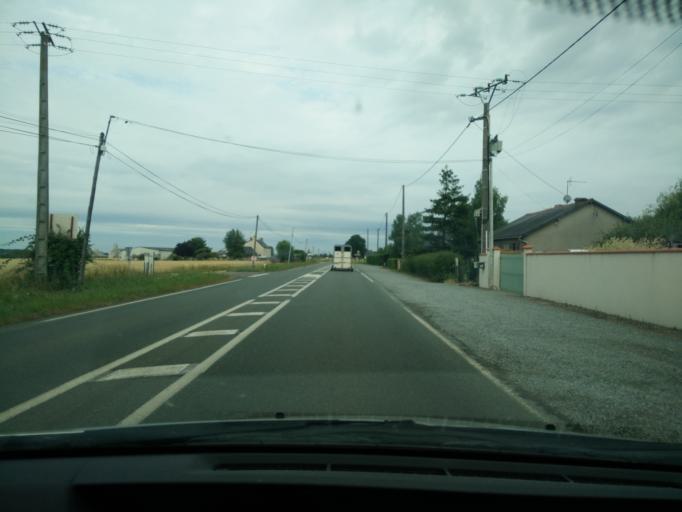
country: FR
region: Pays de la Loire
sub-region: Departement de Maine-et-Loire
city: Brissac-Quince
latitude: 47.3220
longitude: -0.4121
